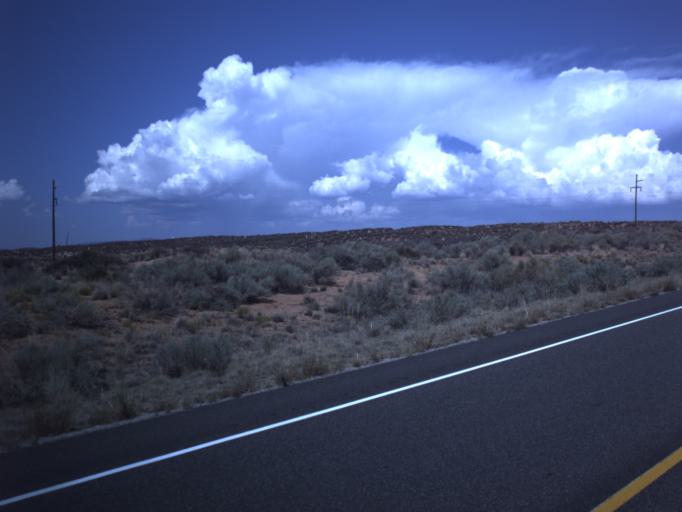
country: US
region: Utah
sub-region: San Juan County
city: Blanding
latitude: 37.3472
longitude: -109.5191
